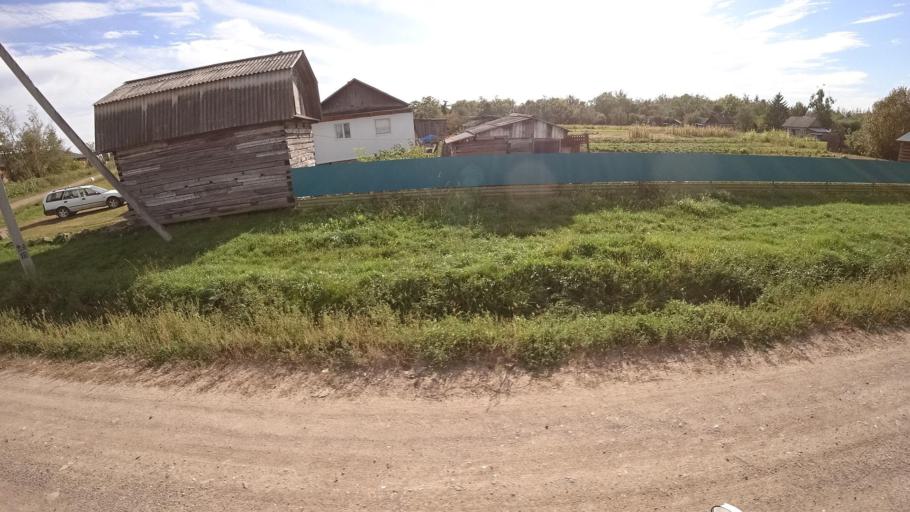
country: RU
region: Primorskiy
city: Dostoyevka
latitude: 44.3041
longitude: 133.4554
